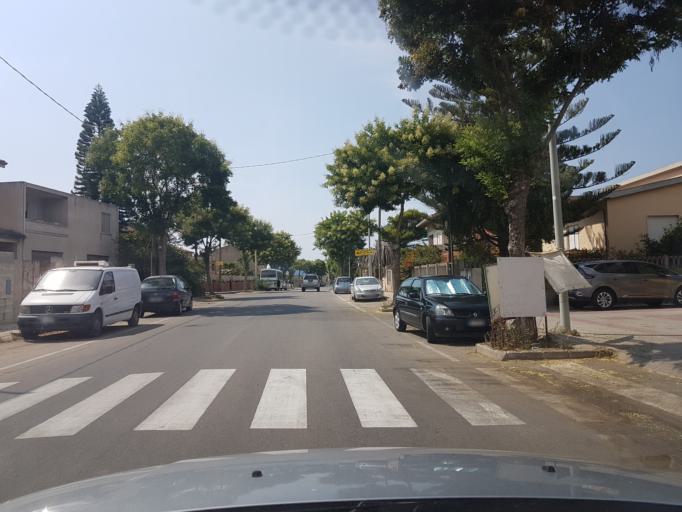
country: IT
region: Sardinia
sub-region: Provincia di Oristano
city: Cabras
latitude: 39.9232
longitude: 8.5411
